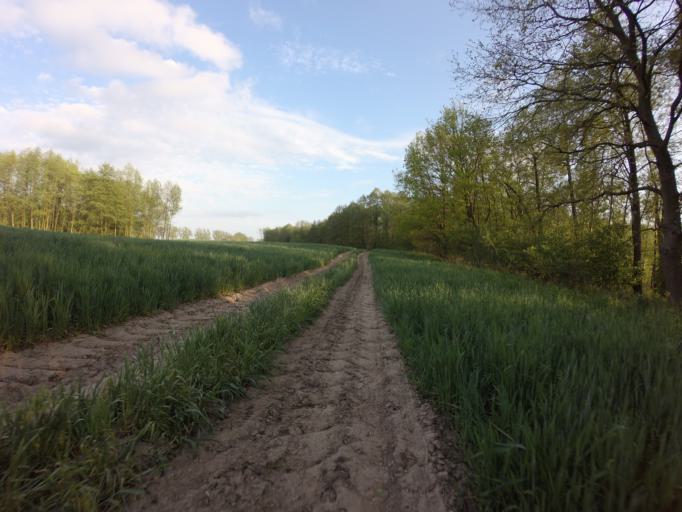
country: PL
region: West Pomeranian Voivodeship
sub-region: Powiat choszczenski
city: Choszczno
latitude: 53.1548
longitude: 15.3445
